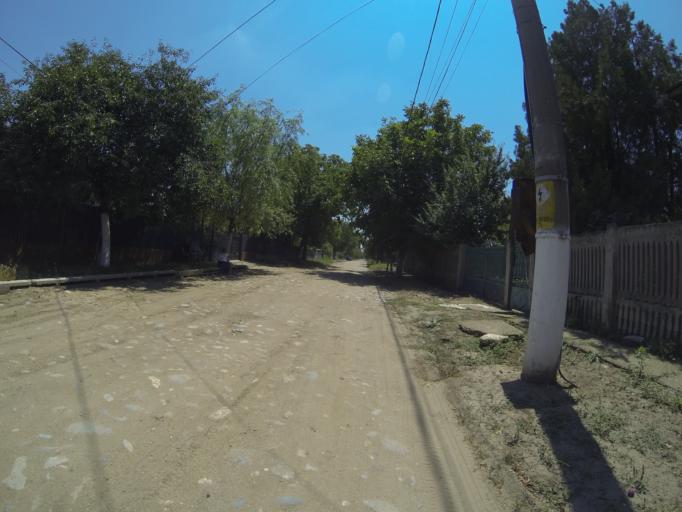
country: RO
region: Dolj
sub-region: Comuna Segarcea
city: Segarcea
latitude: 44.0896
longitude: 23.7430
